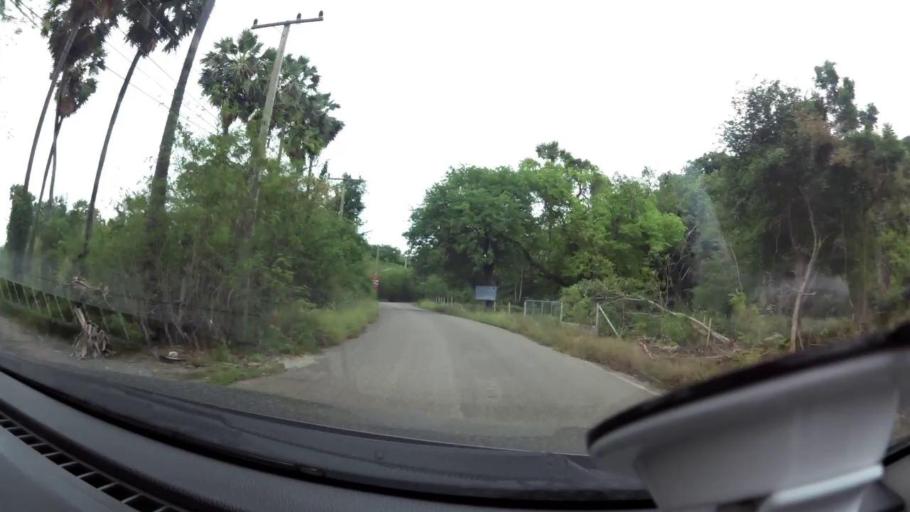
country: TH
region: Prachuap Khiri Khan
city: Pran Buri
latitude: 12.4281
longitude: 99.9789
